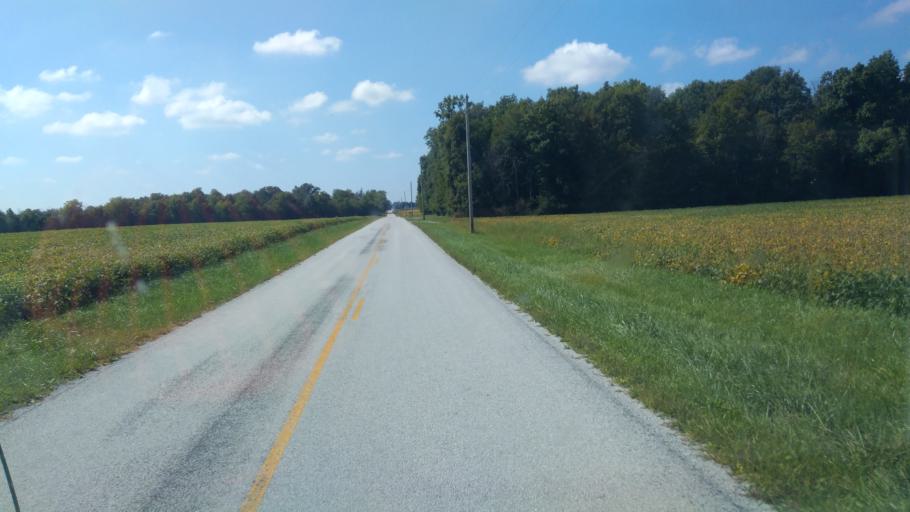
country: US
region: Ohio
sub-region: Hardin County
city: Ada
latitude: 40.7474
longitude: -83.7165
